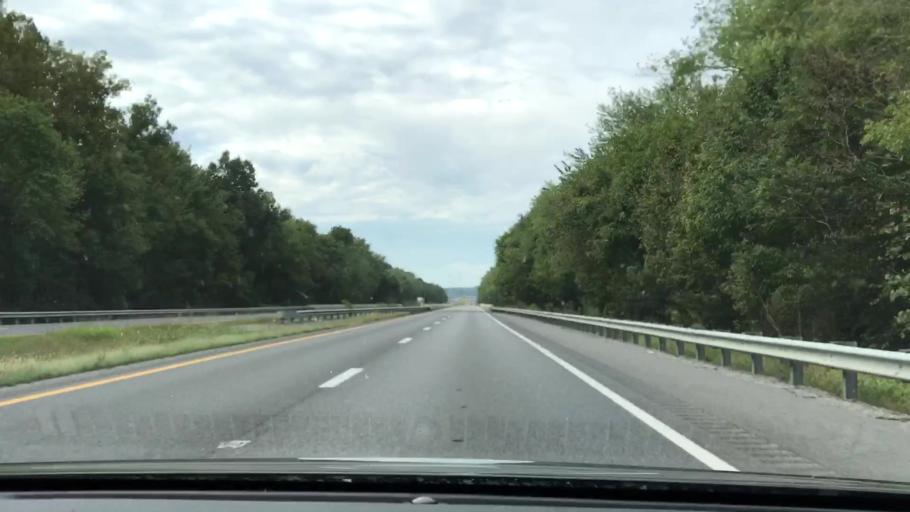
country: US
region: Kentucky
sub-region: Marshall County
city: Benton
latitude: 36.8850
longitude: -88.3553
